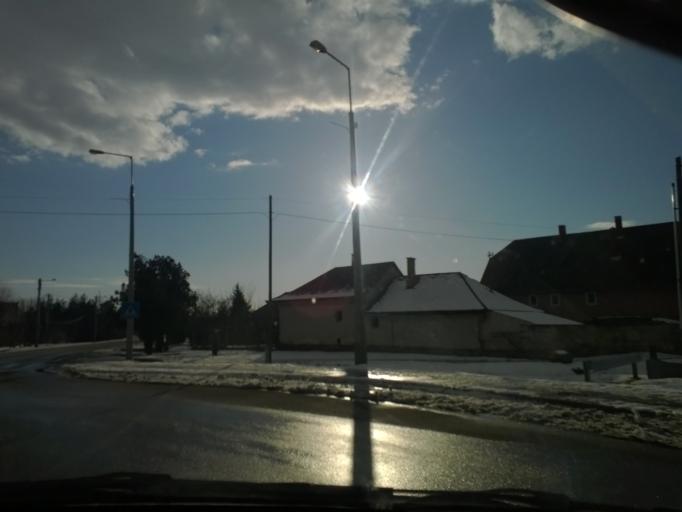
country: HU
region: Fejer
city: Polgardi
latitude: 47.0529
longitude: 18.3043
